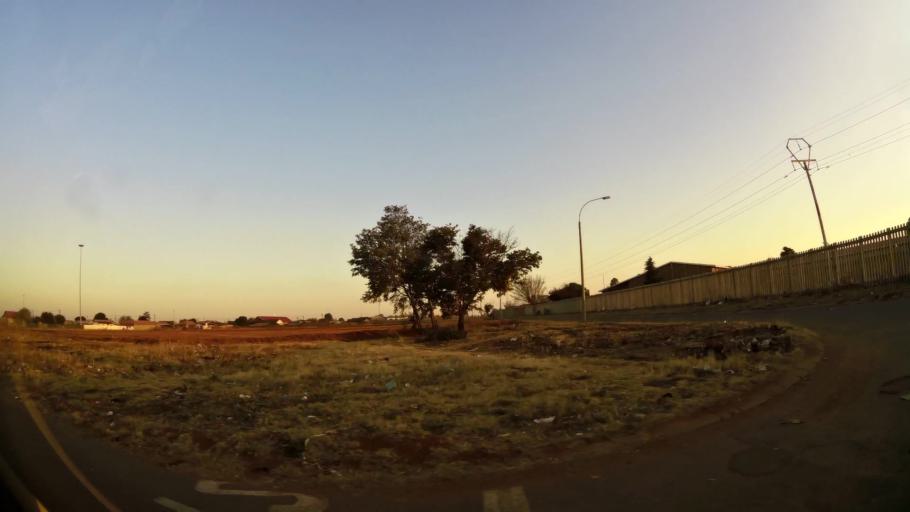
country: ZA
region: Gauteng
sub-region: West Rand District Municipality
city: Randfontein
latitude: -26.1993
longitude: 27.7088
